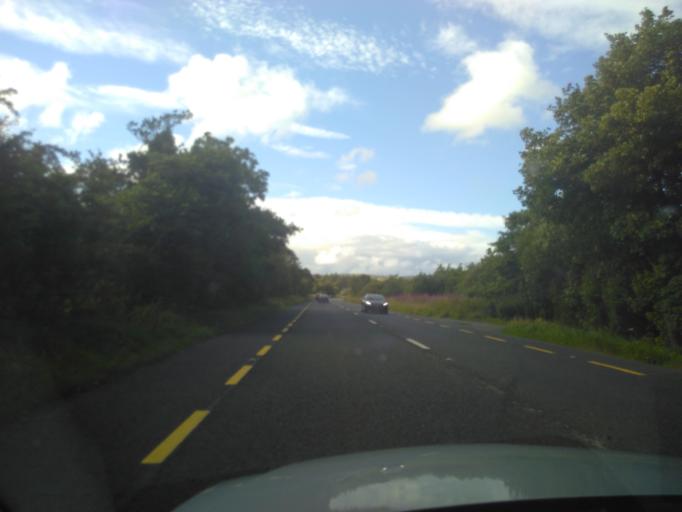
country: IE
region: Ulster
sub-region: County Donegal
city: Ballybofey
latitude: 54.8409
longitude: -7.7493
